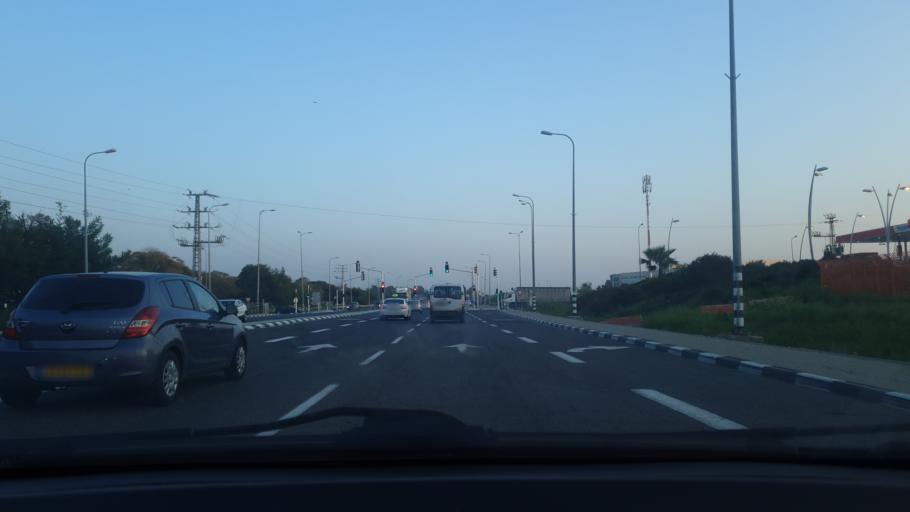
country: IL
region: Central District
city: Kefar Habad
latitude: 31.9607
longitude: 34.8508
